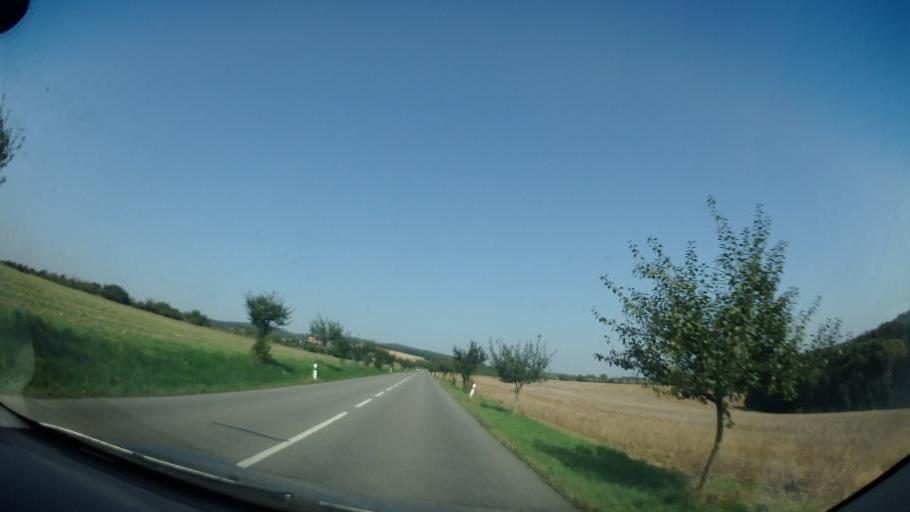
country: CZ
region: South Moravian
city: Kurim
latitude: 49.2479
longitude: 16.5281
